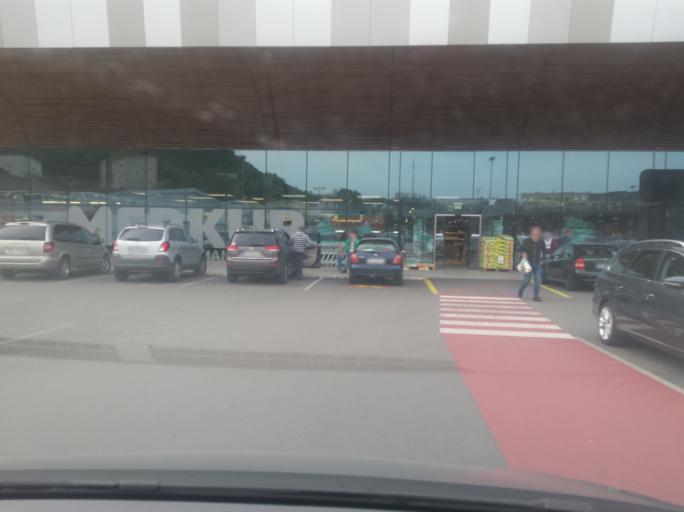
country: AT
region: Lower Austria
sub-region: Politischer Bezirk Bruck an der Leitha
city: Hainburg an der Donau
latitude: 48.1487
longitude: 16.9455
